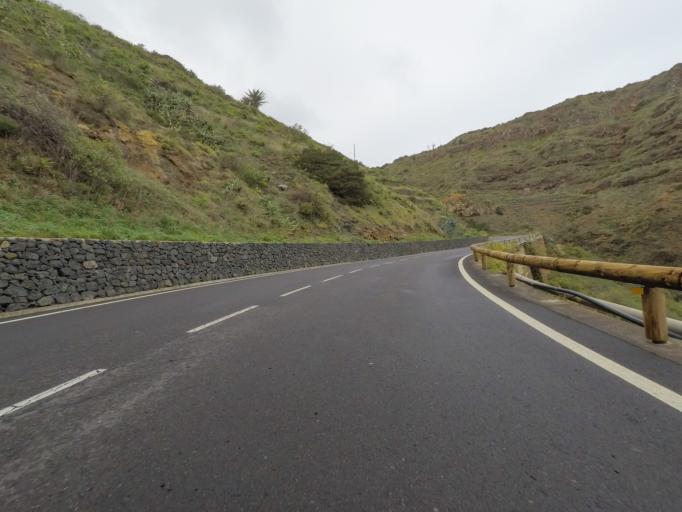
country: ES
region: Canary Islands
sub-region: Provincia de Santa Cruz de Tenerife
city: Agulo
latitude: 28.1871
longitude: -17.2141
